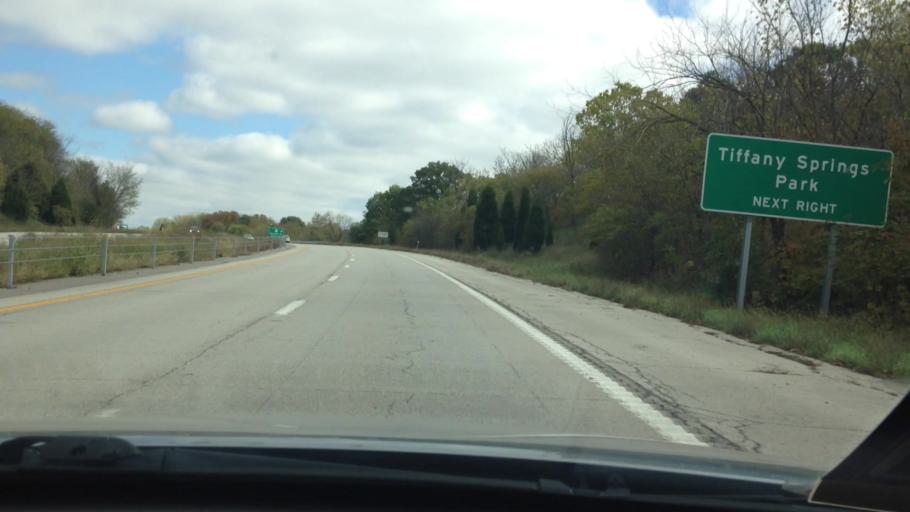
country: US
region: Missouri
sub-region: Platte County
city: Weatherby Lake
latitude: 39.2450
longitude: -94.7442
